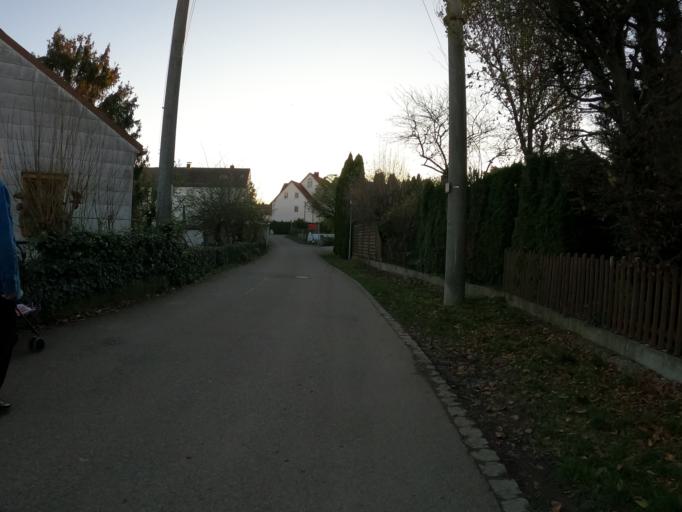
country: DE
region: Bavaria
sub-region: Swabia
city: Holzheim
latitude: 48.4200
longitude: 10.0626
